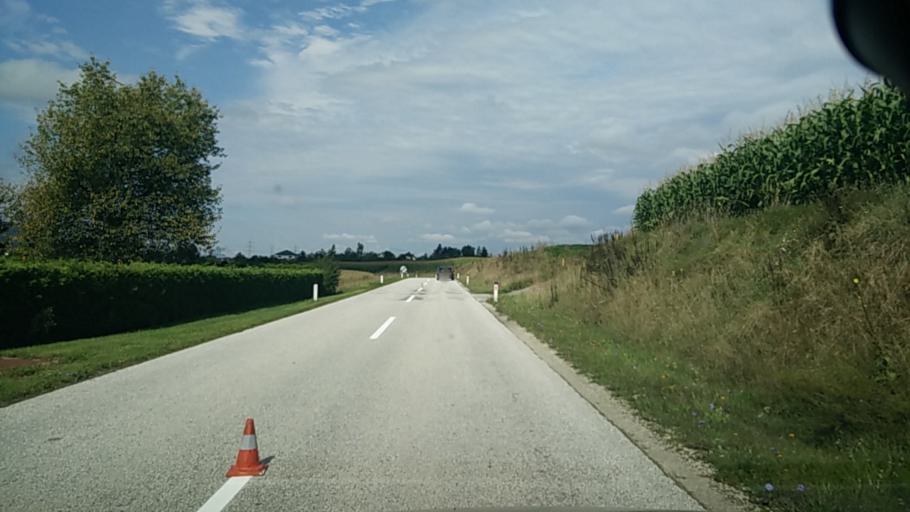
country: AT
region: Carinthia
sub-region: Politischer Bezirk Klagenfurt Land
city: Grafenstein
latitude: 46.6135
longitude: 14.4872
